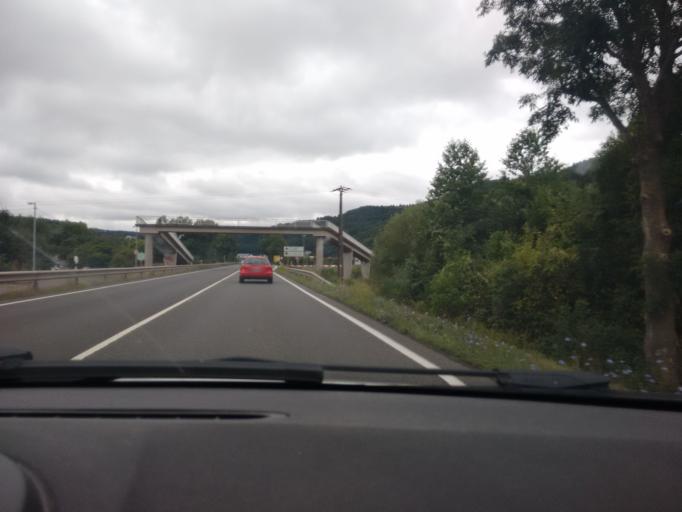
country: DE
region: Rheinland-Pfalz
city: Hintertiefenbach
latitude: 49.7153
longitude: 7.3679
